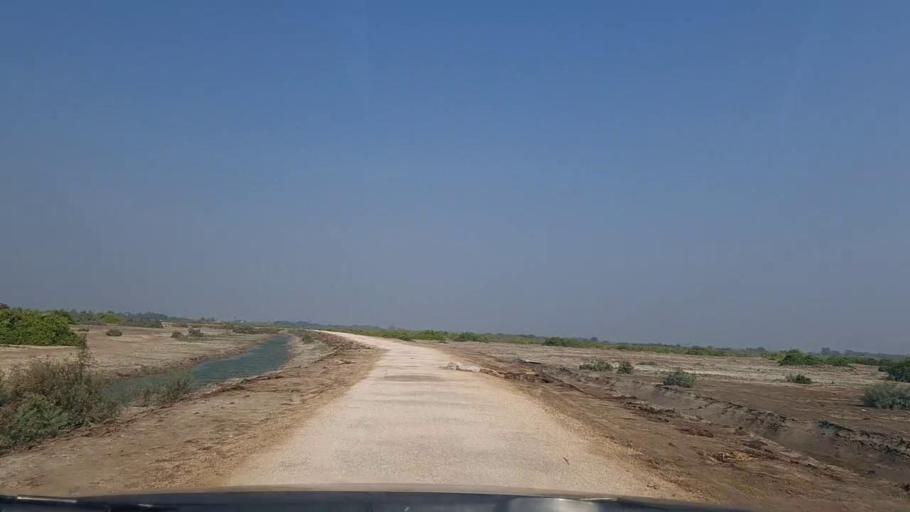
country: PK
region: Sindh
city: Mirpur Sakro
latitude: 24.5766
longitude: 67.7575
